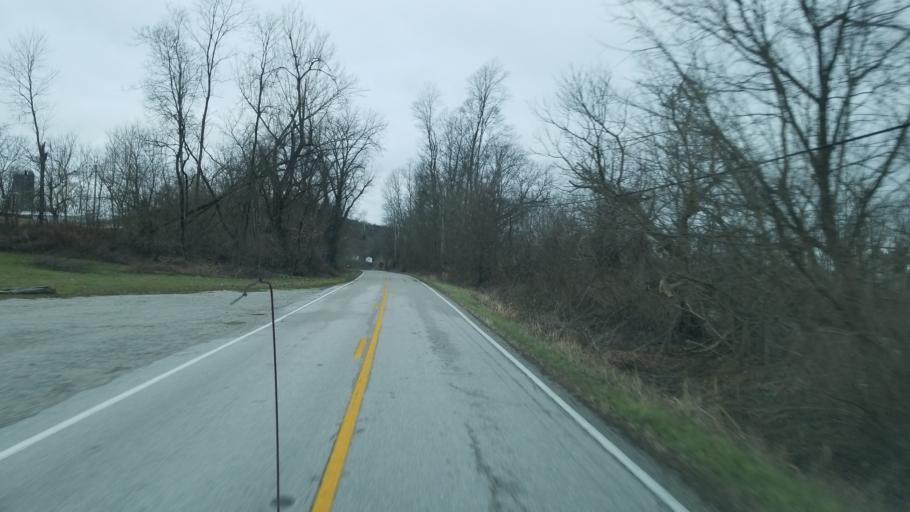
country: US
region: Kentucky
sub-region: Bracken County
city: Brooksville
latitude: 38.7894
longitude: -84.1703
